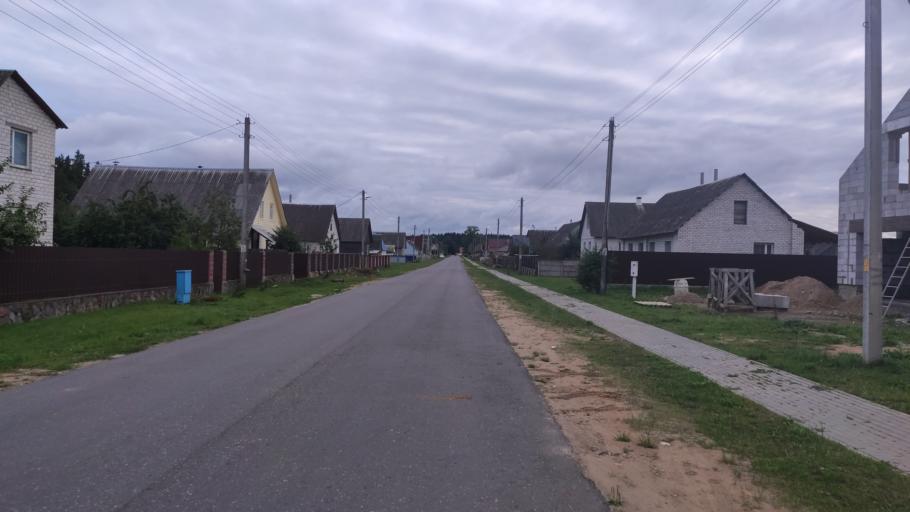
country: BY
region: Minsk
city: Narach
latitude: 54.9290
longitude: 26.6966
